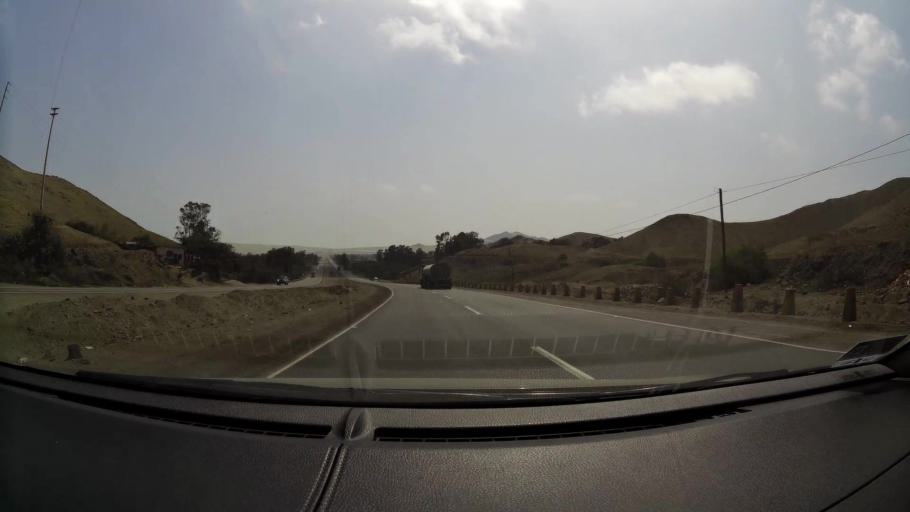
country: PE
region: Lima
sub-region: Provincia de Huaral
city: Huaral
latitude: -11.4610
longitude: -77.3134
